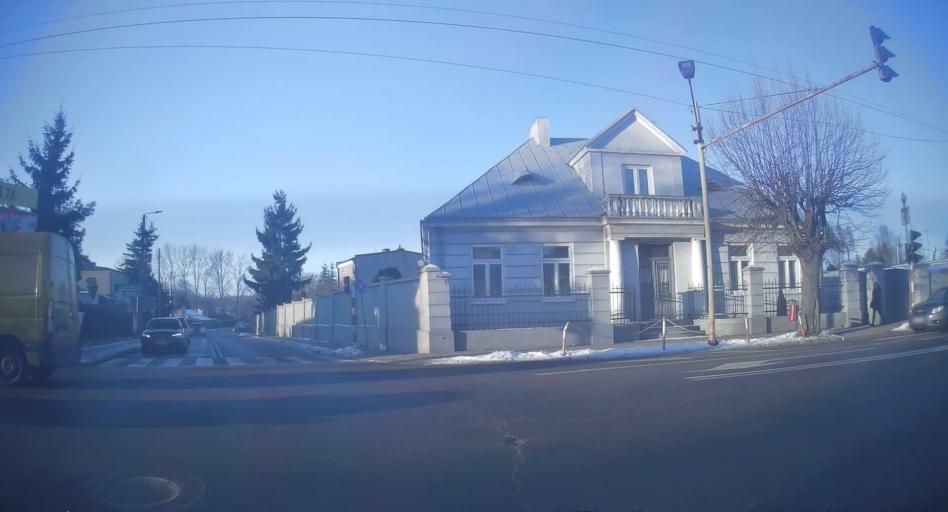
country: PL
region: Lodz Voivodeship
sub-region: Powiat rawski
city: Rawa Mazowiecka
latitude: 51.7631
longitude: 20.2488
